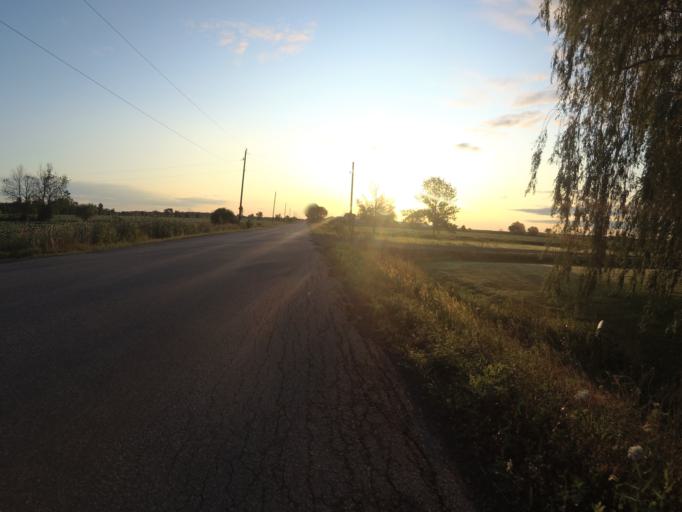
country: CA
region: Ontario
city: Ottawa
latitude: 45.1046
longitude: -75.5490
